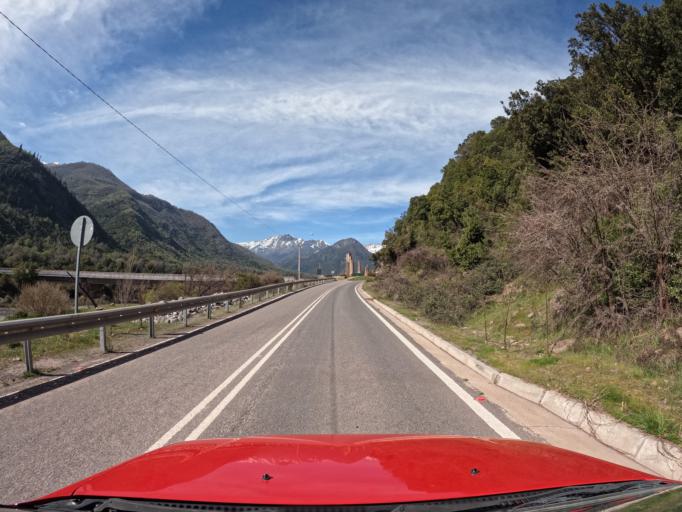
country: CL
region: O'Higgins
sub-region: Provincia de Colchagua
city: Chimbarongo
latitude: -35.0003
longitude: -70.7945
